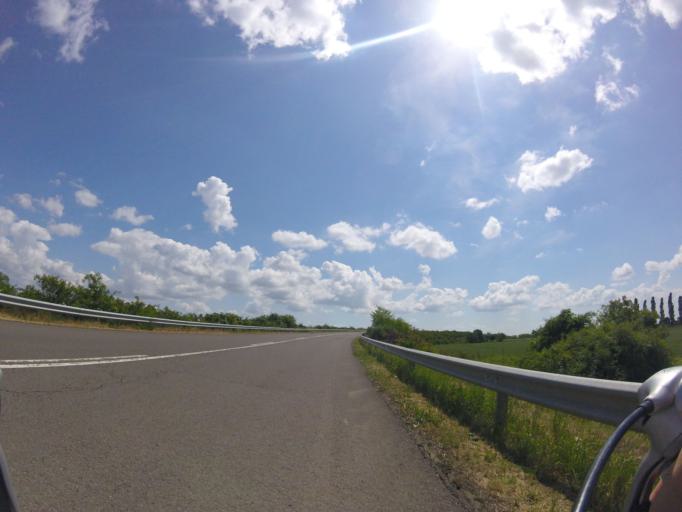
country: HU
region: Heves
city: Karacsond
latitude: 47.7060
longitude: 20.0603
